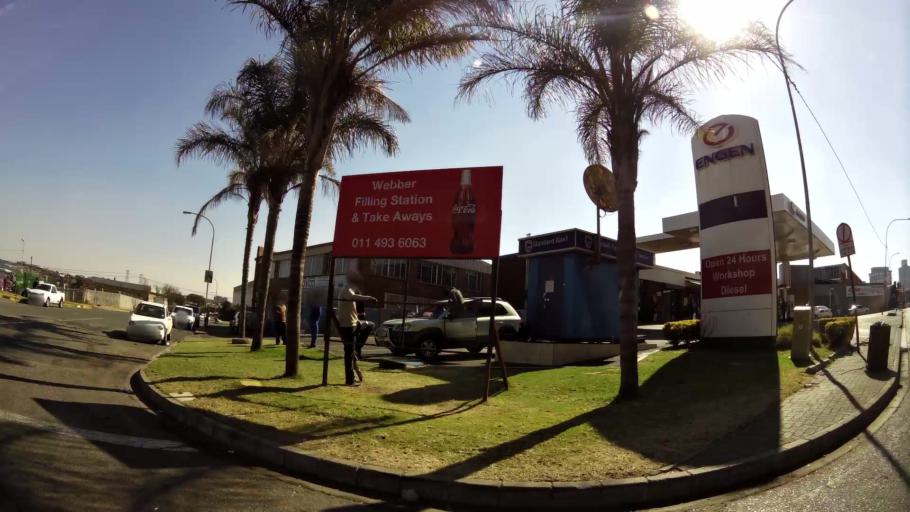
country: ZA
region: Gauteng
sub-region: City of Johannesburg Metropolitan Municipality
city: Johannesburg
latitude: -26.2157
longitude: 28.0337
